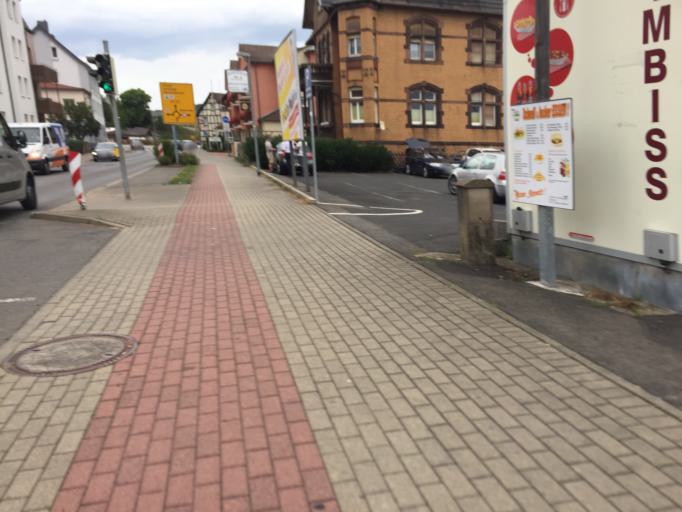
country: DE
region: Hesse
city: Bebra
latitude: 50.9661
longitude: 9.7958
